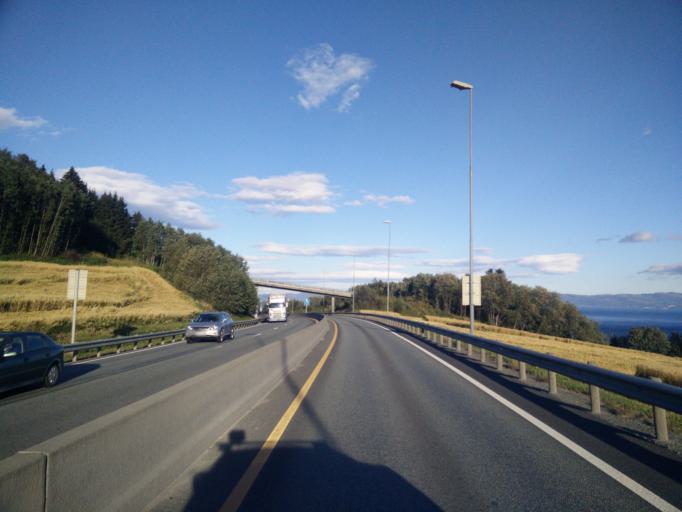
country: NO
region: Sor-Trondelag
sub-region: Malvik
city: Malvik
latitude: 63.4247
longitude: 10.5741
